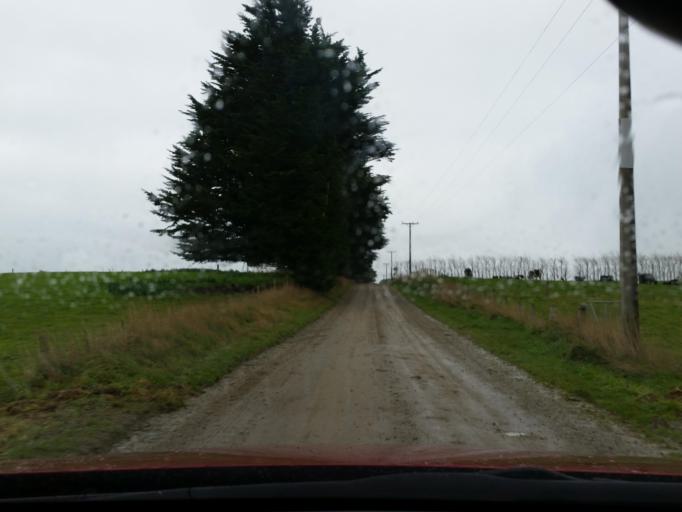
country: NZ
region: Southland
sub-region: Invercargill City
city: Invercargill
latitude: -46.3176
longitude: 168.4789
